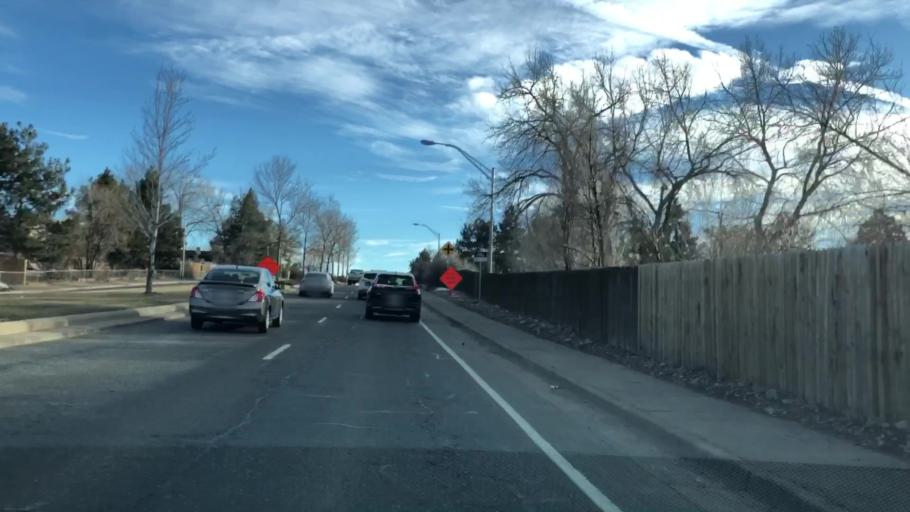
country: US
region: Colorado
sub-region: Adams County
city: Aurora
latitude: 39.6585
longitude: -104.7914
